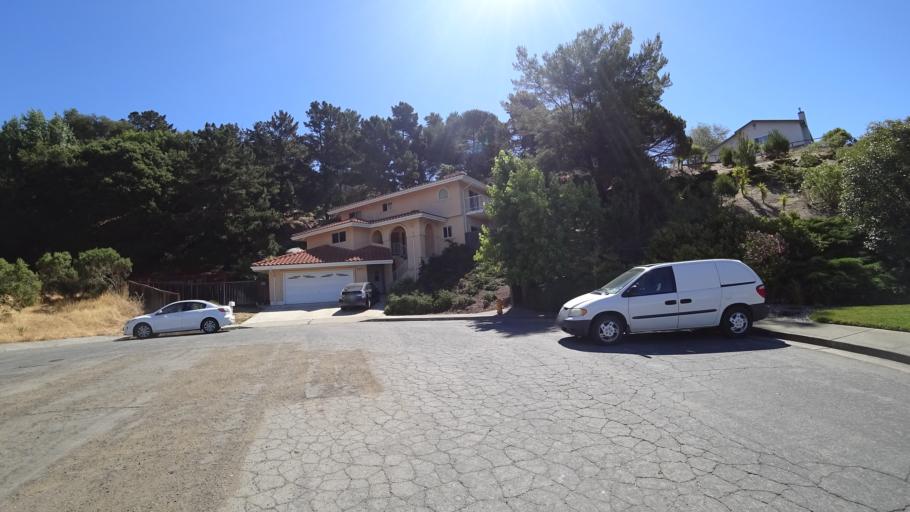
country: US
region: California
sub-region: Alameda County
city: Fairview
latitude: 37.6475
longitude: -122.0318
